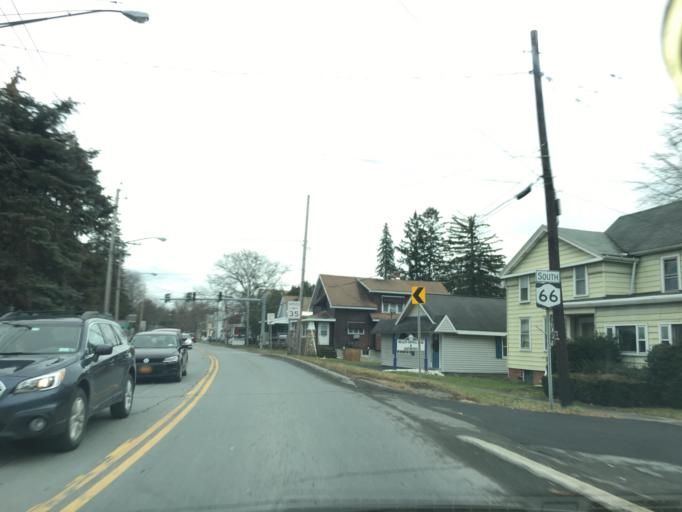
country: US
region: New York
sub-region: Rensselaer County
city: Wynantskill
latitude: 42.6934
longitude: -73.6346
